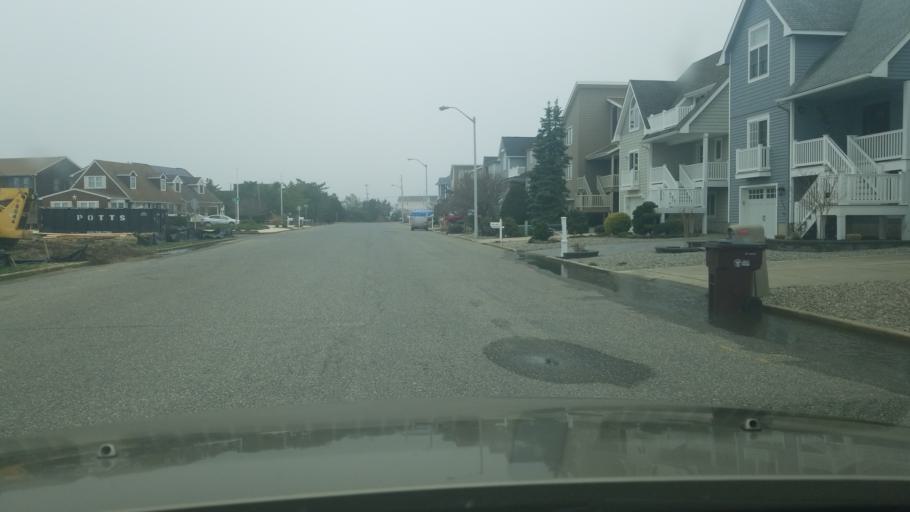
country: US
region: New Jersey
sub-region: Ocean County
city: Seaside Park
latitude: 39.9122
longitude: -74.0847
